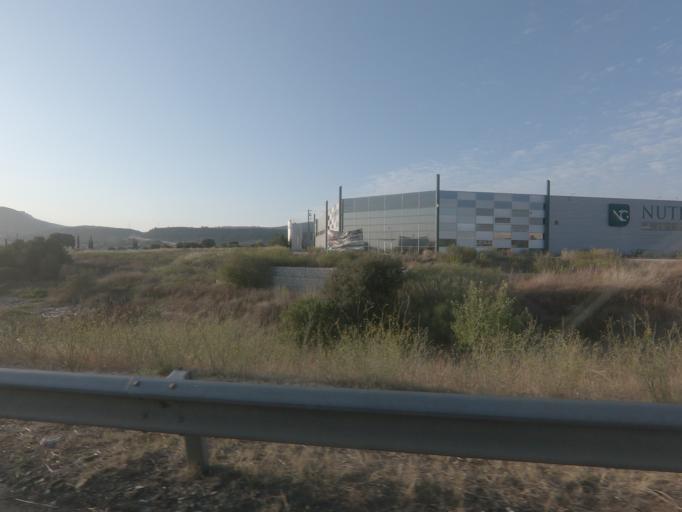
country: PT
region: Santarem
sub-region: Alcanena
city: Alcanena
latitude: 39.4776
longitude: -8.6302
